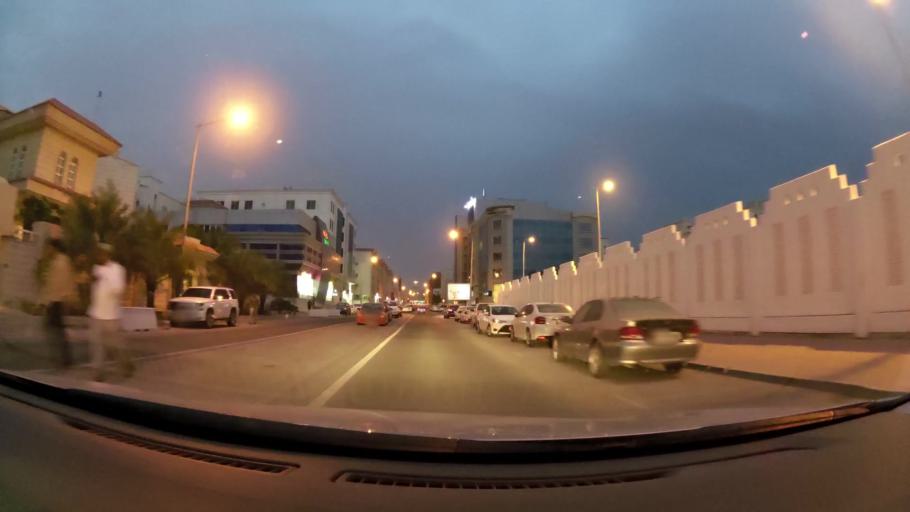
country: QA
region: Baladiyat ad Dawhah
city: Doha
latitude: 25.2662
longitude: 51.5196
